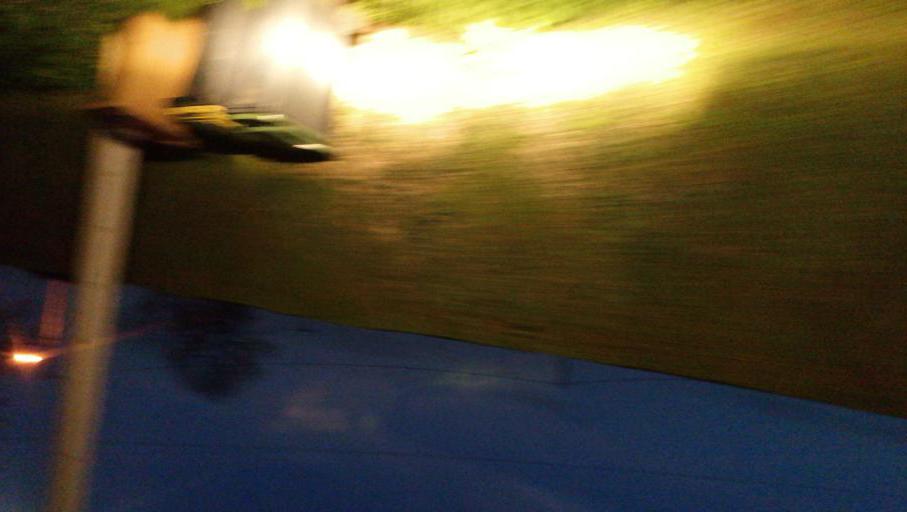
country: FR
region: Brittany
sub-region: Departement des Cotes-d'Armor
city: Plouha
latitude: 48.6703
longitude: -2.9602
